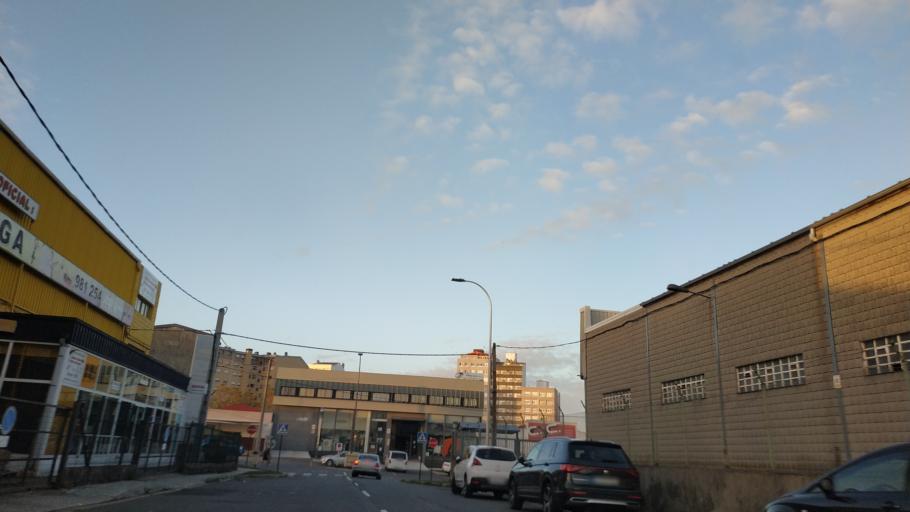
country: ES
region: Galicia
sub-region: Provincia da Coruna
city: A Coruna
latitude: 43.3556
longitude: -8.4196
